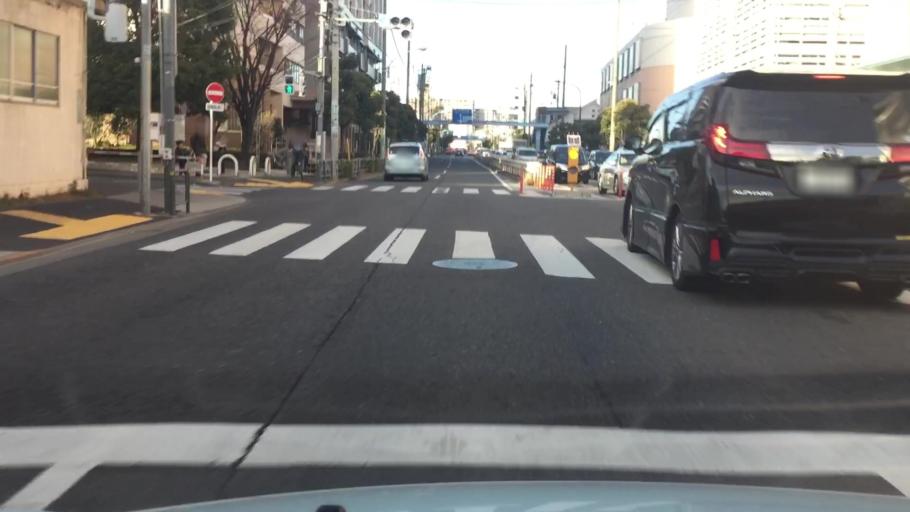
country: JP
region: Saitama
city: Soka
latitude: 35.7740
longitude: 139.7846
